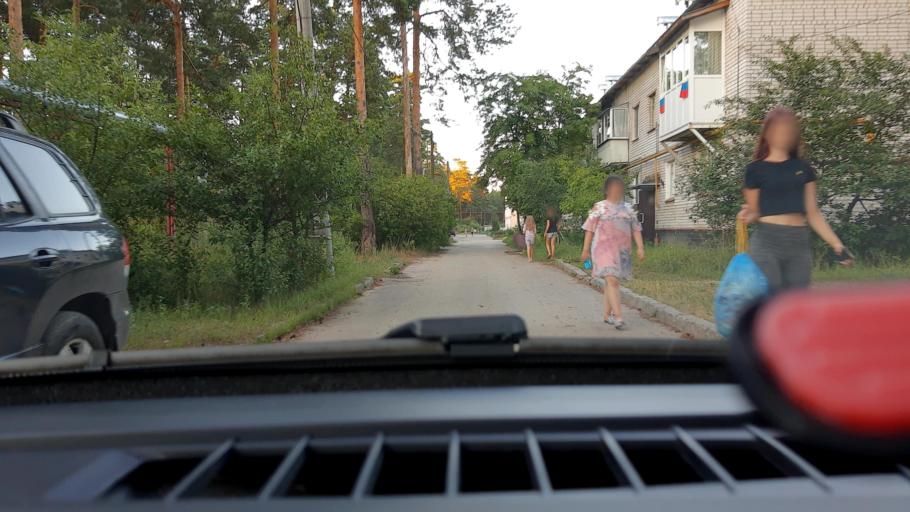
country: RU
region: Nizjnij Novgorod
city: Lukino
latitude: 56.3938
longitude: 43.7194
